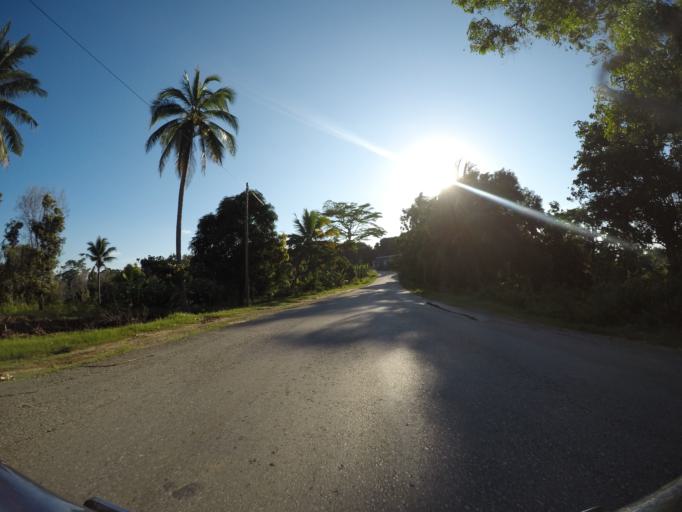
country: TZ
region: Pemba South
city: Mtambile
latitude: -5.3756
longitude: 39.7046
